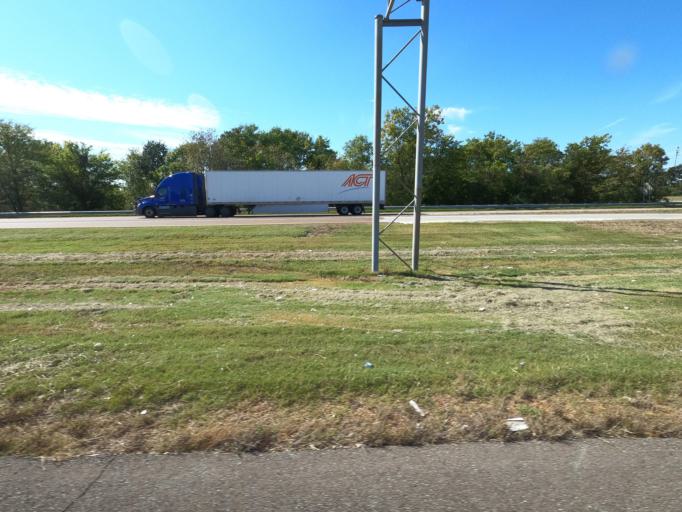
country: US
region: Tennessee
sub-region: Dyer County
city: Dyersburg
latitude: 36.0707
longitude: -89.3460
